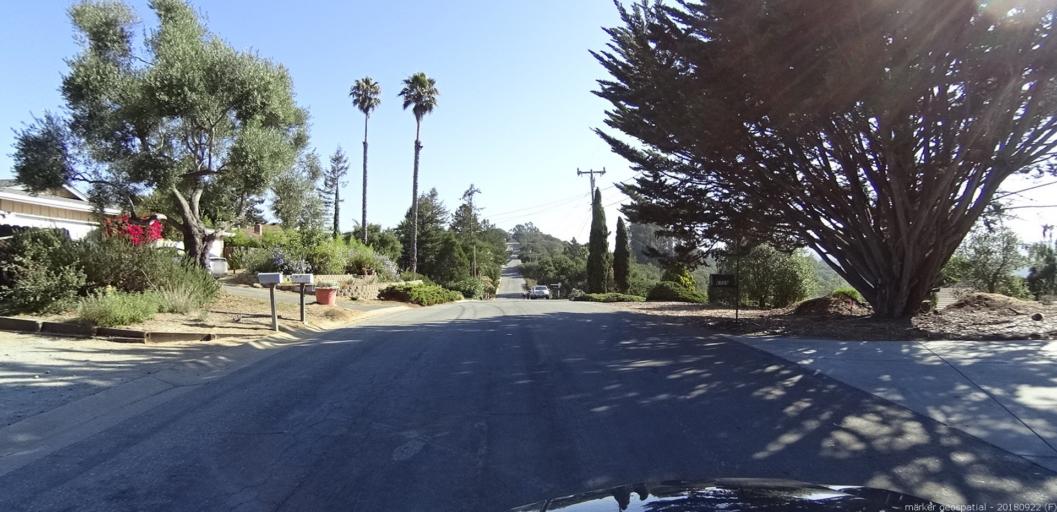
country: US
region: California
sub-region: Monterey County
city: Prunedale
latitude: 36.8191
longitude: -121.6435
